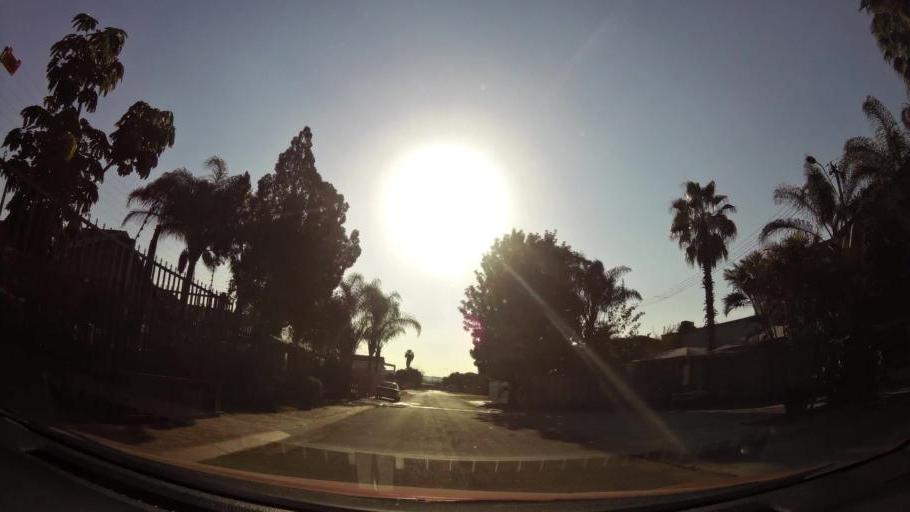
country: ZA
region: North-West
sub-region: Bojanala Platinum District Municipality
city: Rustenburg
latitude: -25.6436
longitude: 27.2406
